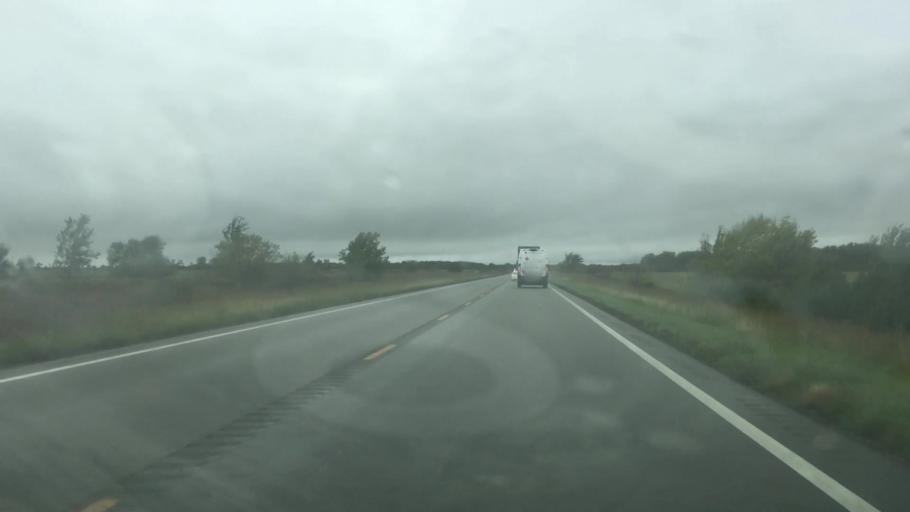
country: US
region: Kansas
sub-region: Anderson County
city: Garnett
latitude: 38.1369
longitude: -95.3321
